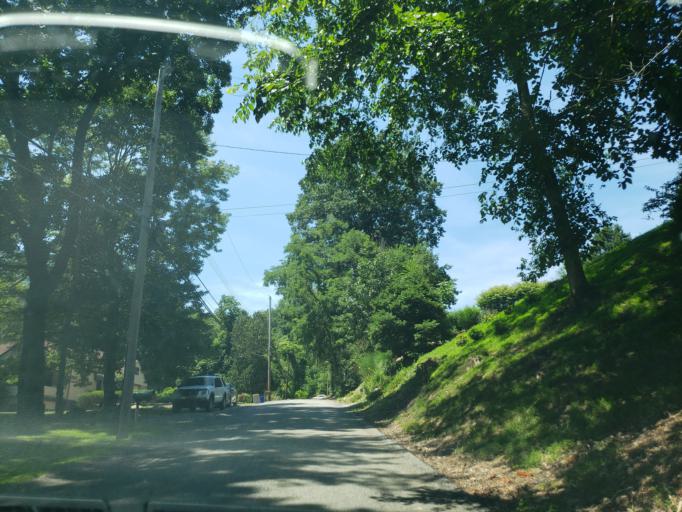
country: US
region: Pennsylvania
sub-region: Allegheny County
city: Emsworth
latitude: 40.5174
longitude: -80.0987
